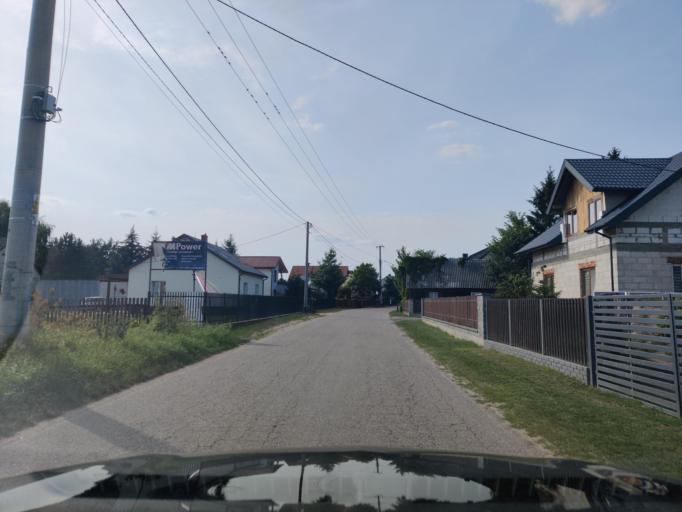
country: PL
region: Masovian Voivodeship
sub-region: Powiat wyszkowski
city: Rzasnik
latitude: 52.7398
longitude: 21.3345
